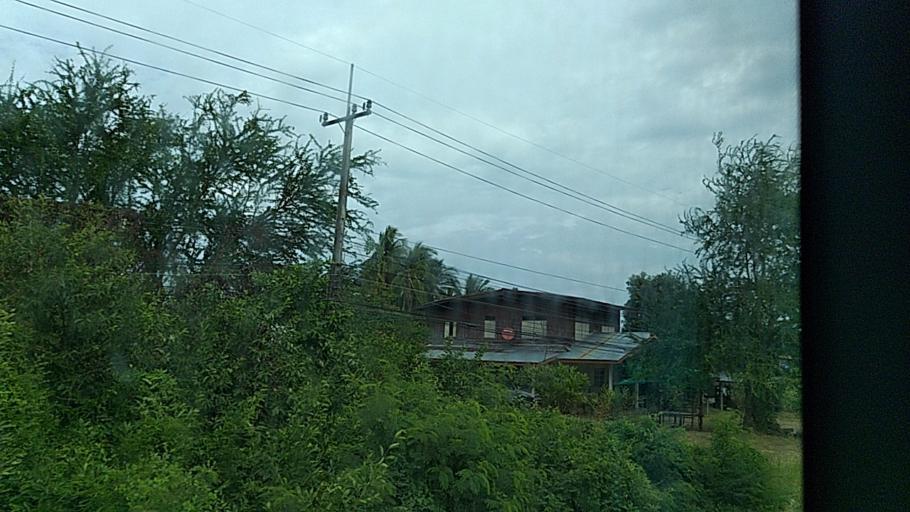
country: TH
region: Maha Sarakham
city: Maha Sarakham
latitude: 16.1489
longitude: 103.3965
